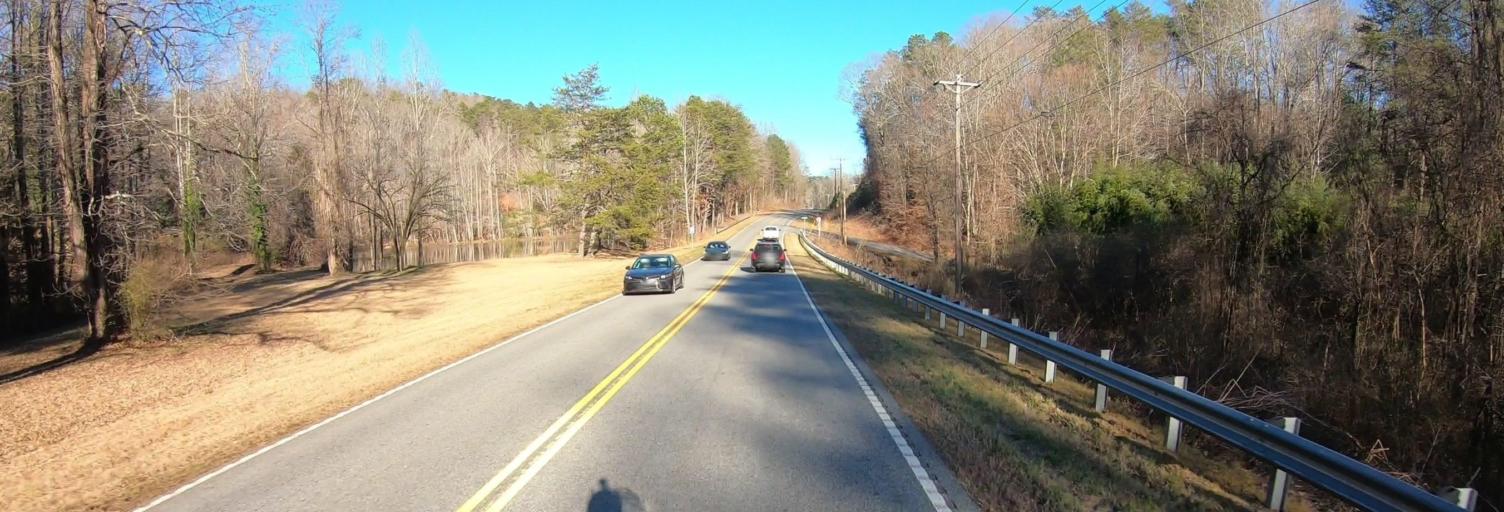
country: US
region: South Carolina
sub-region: Greenville County
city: Tigerville
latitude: 35.0918
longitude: -82.4359
